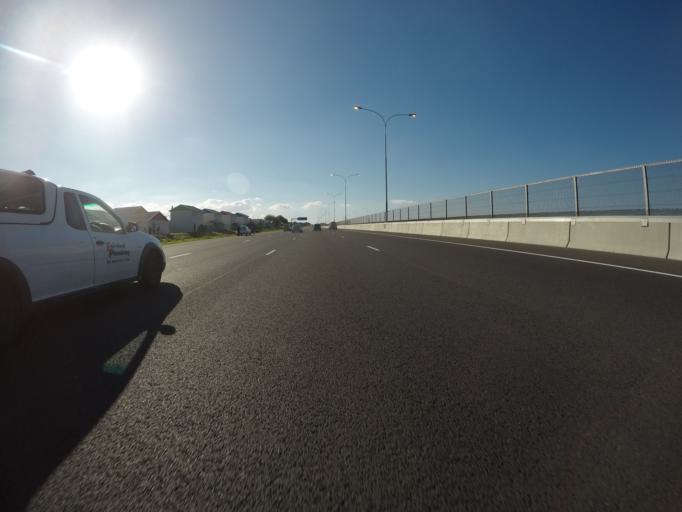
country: ZA
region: Western Cape
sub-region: City of Cape Town
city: Kraaifontein
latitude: -33.9620
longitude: 18.6557
